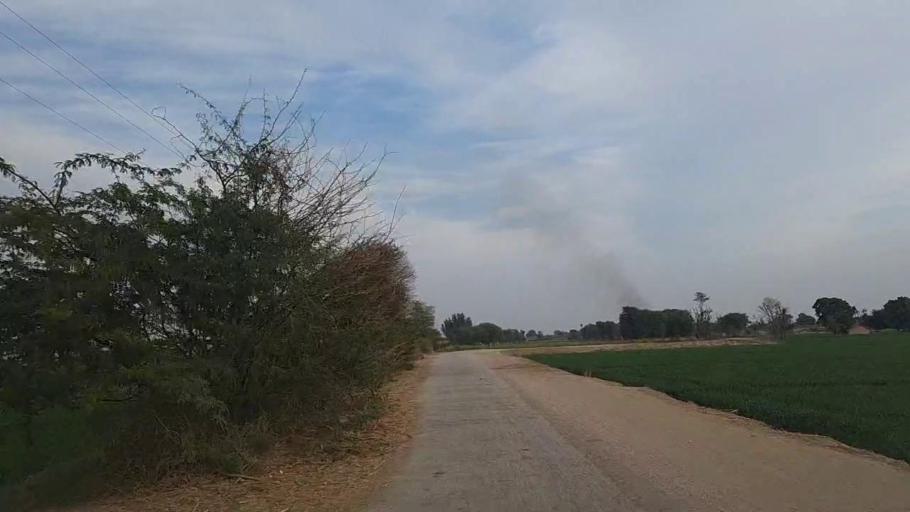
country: PK
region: Sindh
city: Daur
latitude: 26.5282
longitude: 68.4248
